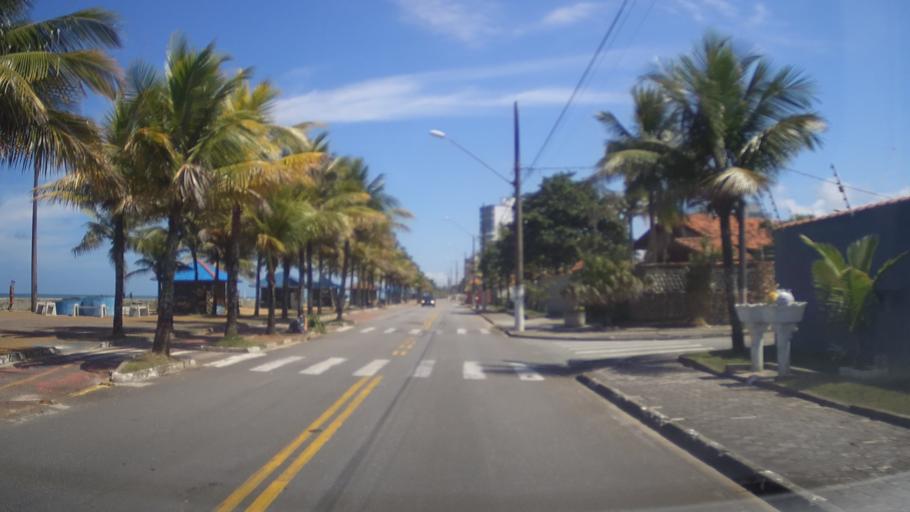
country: BR
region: Sao Paulo
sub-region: Mongagua
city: Mongagua
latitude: -24.1056
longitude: -46.6392
